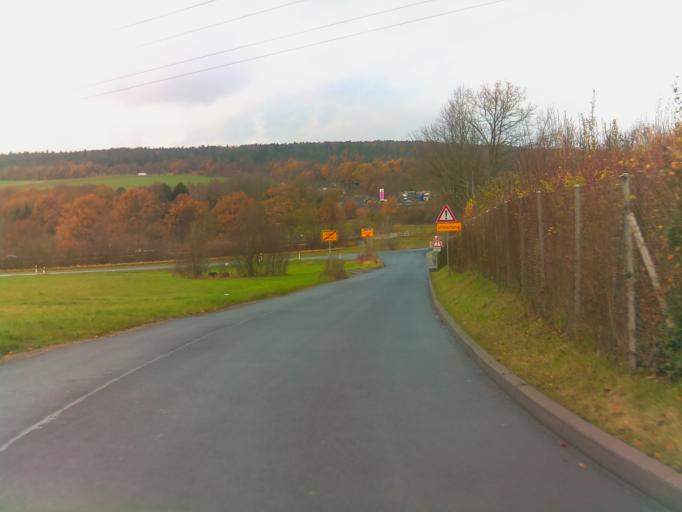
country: DE
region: Hesse
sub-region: Regierungsbezirk Kassel
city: Petersberg
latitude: 50.5760
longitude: 9.7061
